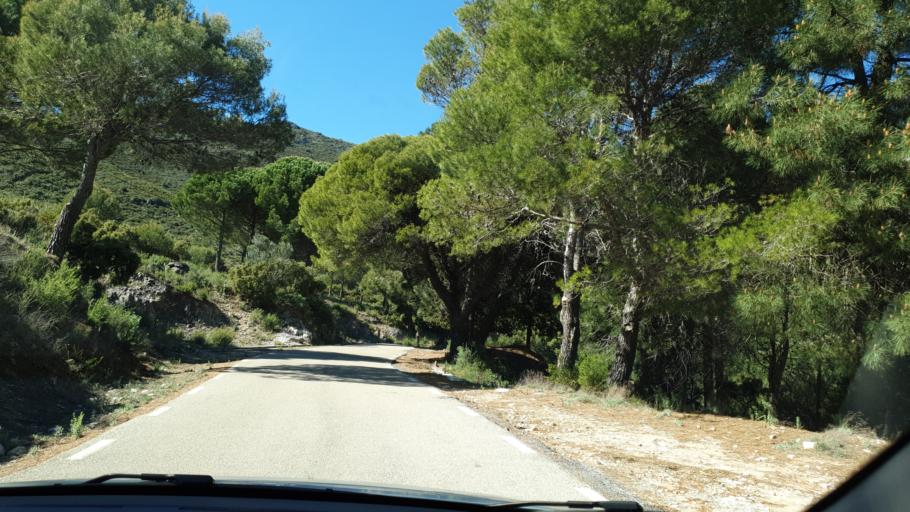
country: ES
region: Andalusia
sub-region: Provincia de Malaga
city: Ojen
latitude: 36.5873
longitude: -4.8683
